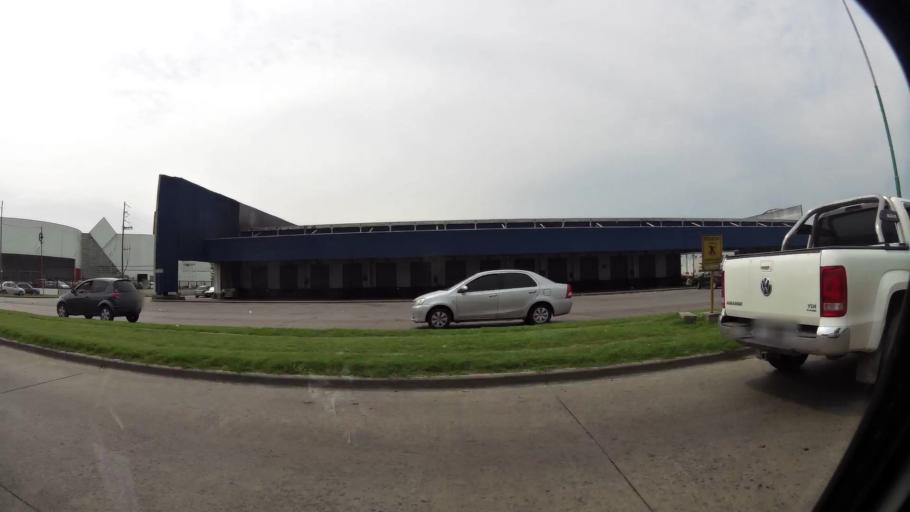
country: AR
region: Buenos Aires
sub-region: Partido de La Plata
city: La Plata
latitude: -34.9057
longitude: -57.9993
